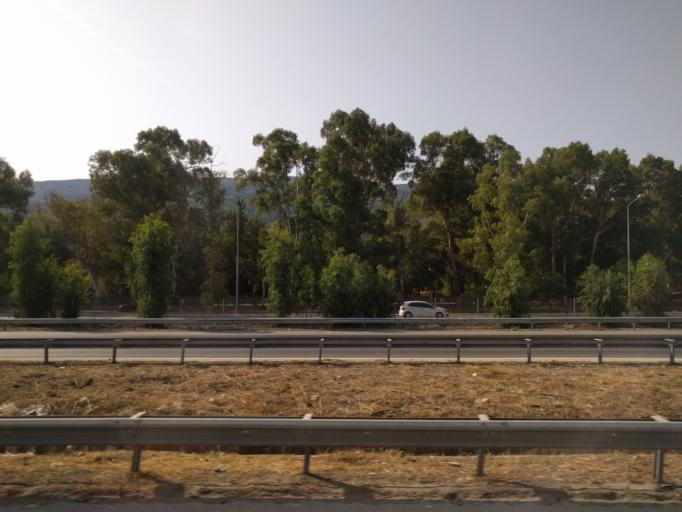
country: TR
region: Izmir
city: Karsiyaka
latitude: 38.3954
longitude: 26.9762
